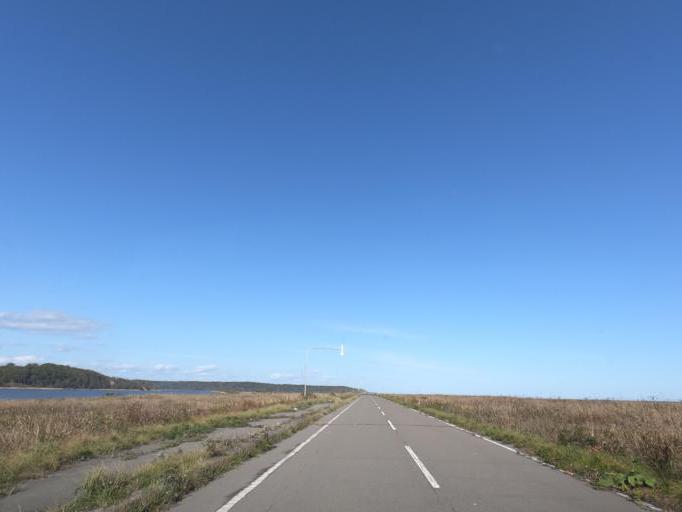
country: JP
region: Hokkaido
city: Obihiro
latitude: 42.5838
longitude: 143.5330
